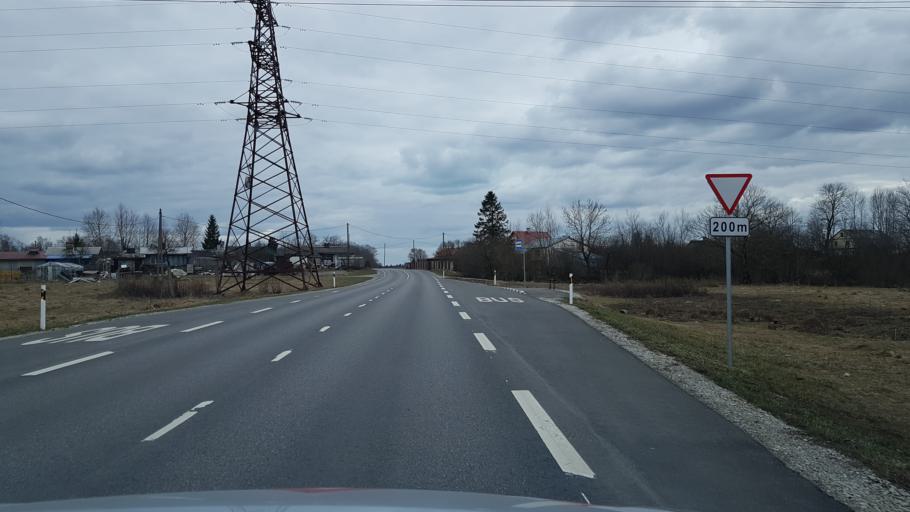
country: EE
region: Ida-Virumaa
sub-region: Narva-Joesuu linn
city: Narva-Joesuu
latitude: 59.4033
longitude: 28.0662
